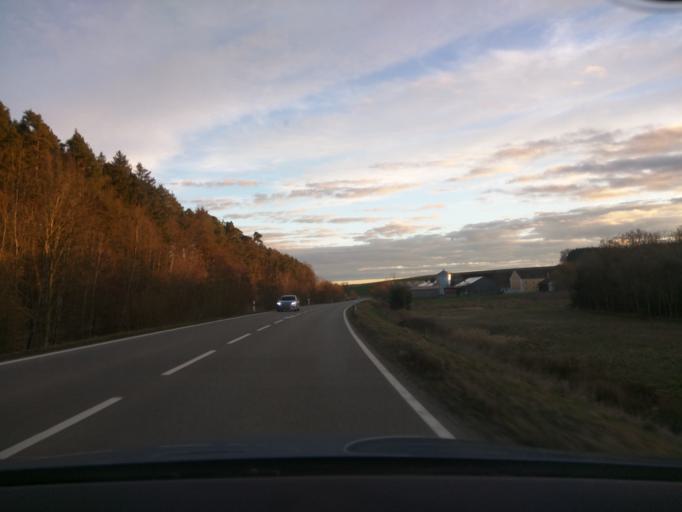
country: DE
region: Bavaria
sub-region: Upper Bavaria
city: Zolling
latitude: 48.4701
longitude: 11.7634
